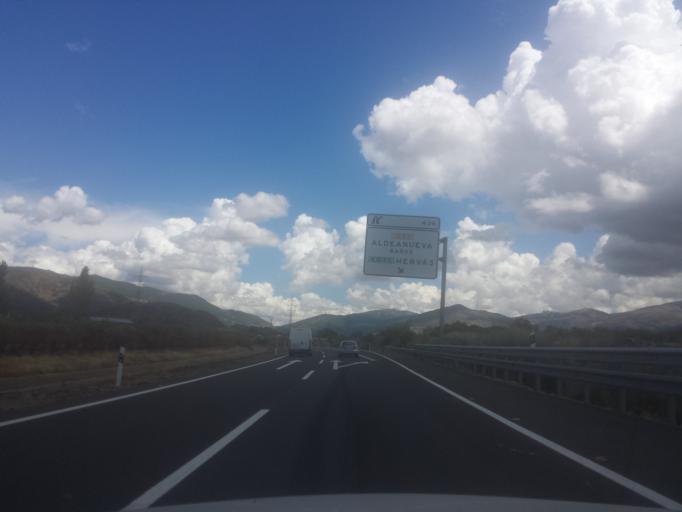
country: ES
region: Extremadura
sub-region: Provincia de Caceres
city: Aldeanueva del Camino
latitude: 40.2595
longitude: -5.9179
